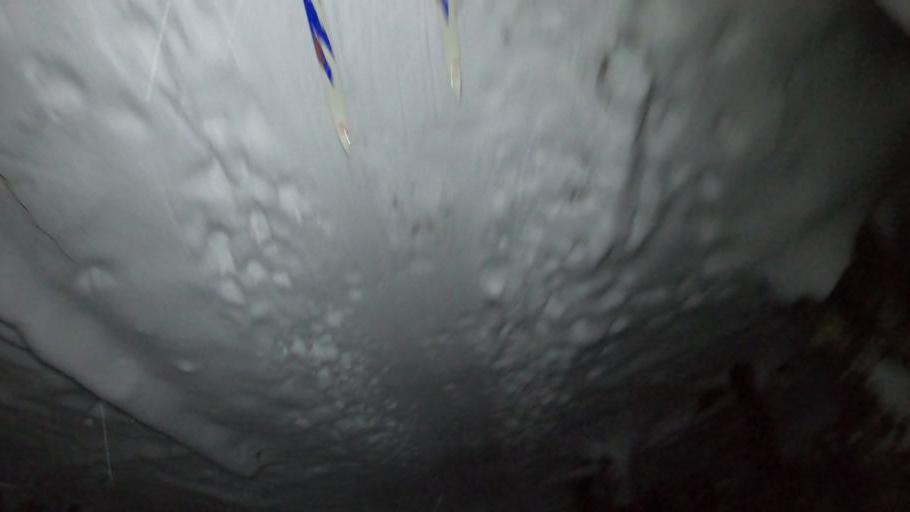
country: RU
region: Moskovskaya
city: Nakhabino
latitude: 55.8838
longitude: 37.2180
